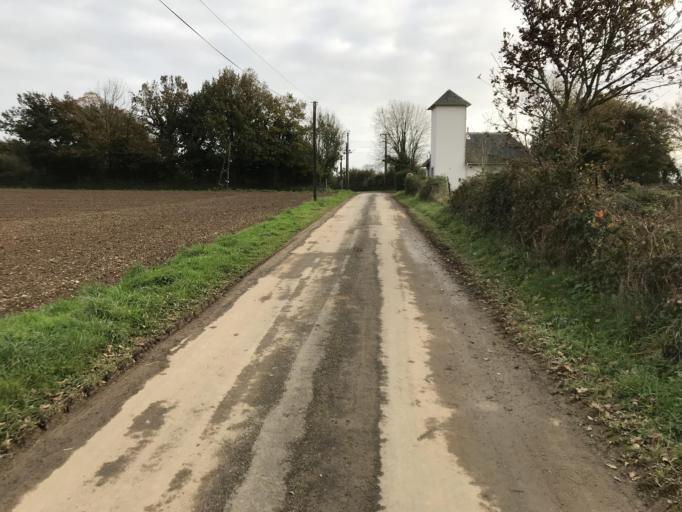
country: FR
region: Brittany
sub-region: Departement du Finistere
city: Hopital-Camfrout
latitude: 48.3267
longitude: -4.2050
